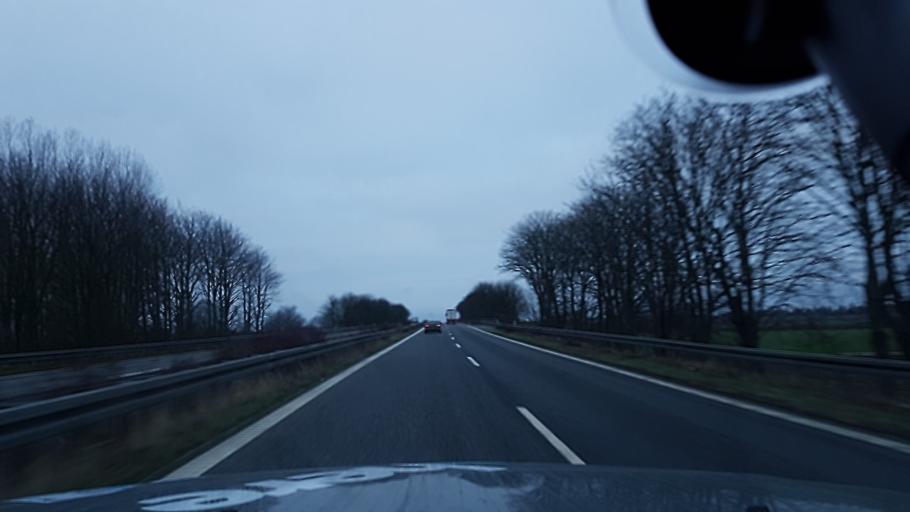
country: DK
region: Zealand
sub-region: Guldborgsund Kommune
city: Sakskobing
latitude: 54.7883
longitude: 11.5665
